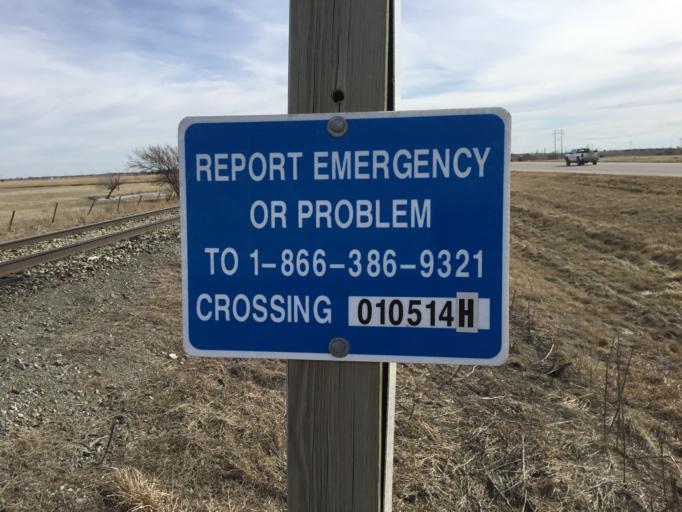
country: US
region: Kansas
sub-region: McPherson County
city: McPherson
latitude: 38.3643
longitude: -97.7591
